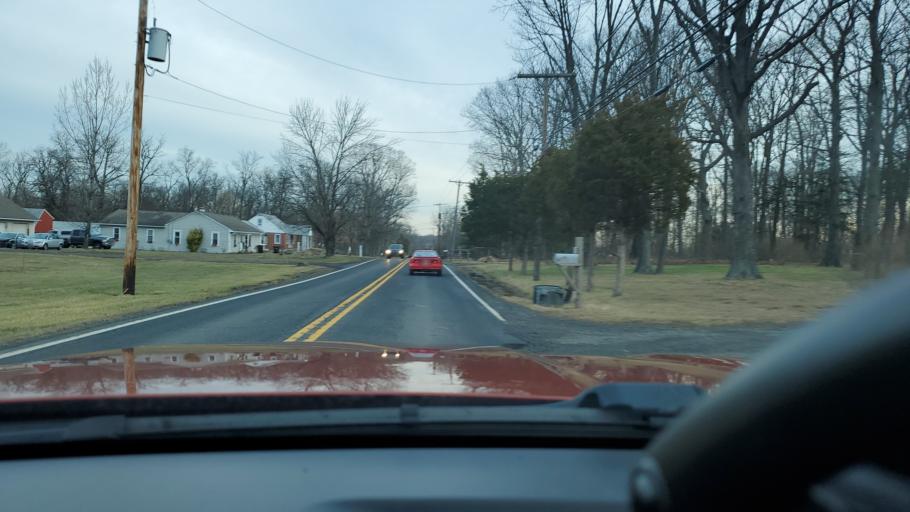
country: US
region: Pennsylvania
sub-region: Montgomery County
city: Woxall
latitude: 40.3256
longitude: -75.4182
